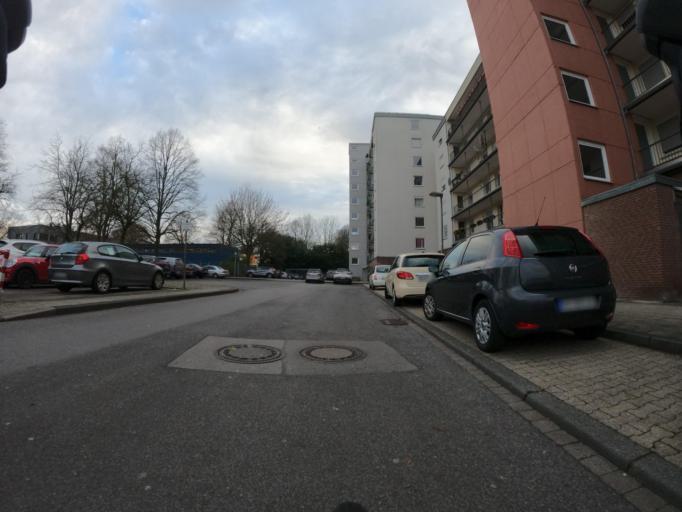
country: DE
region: North Rhine-Westphalia
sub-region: Regierungsbezirk Koln
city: Wurselen
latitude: 50.7544
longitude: 6.1442
